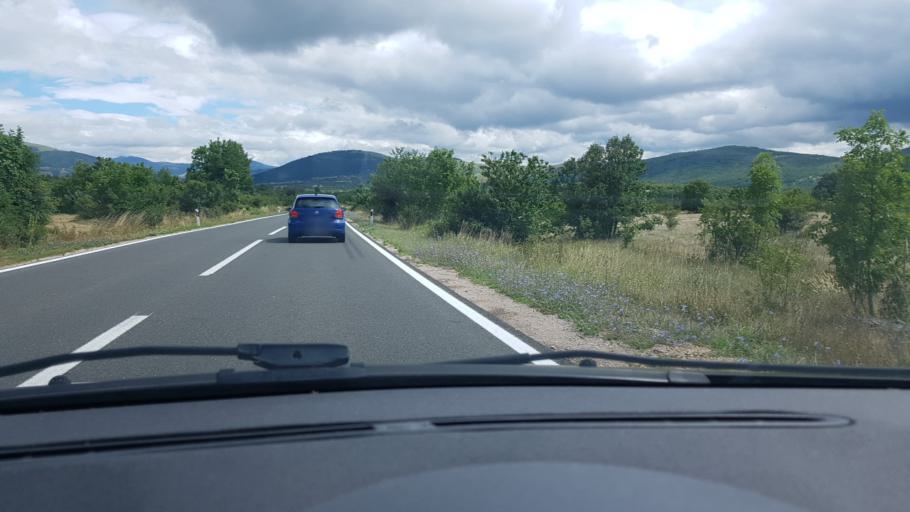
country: HR
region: Zadarska
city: Gracac
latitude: 44.4418
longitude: 15.8536
